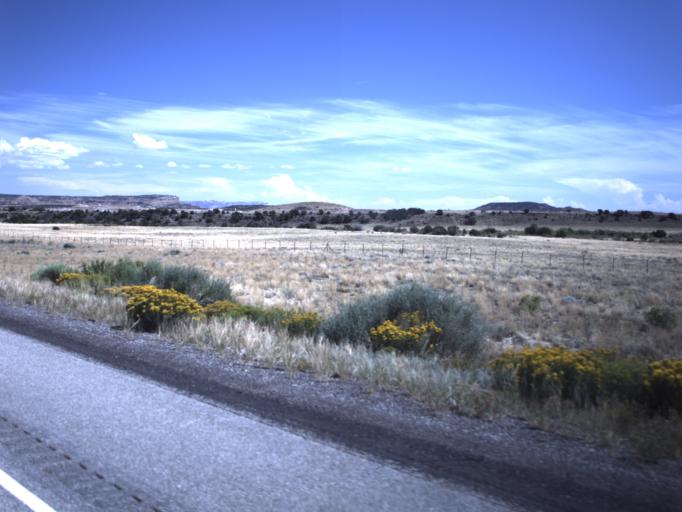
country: US
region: Utah
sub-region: Emery County
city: Ferron
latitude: 38.7754
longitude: -111.3230
